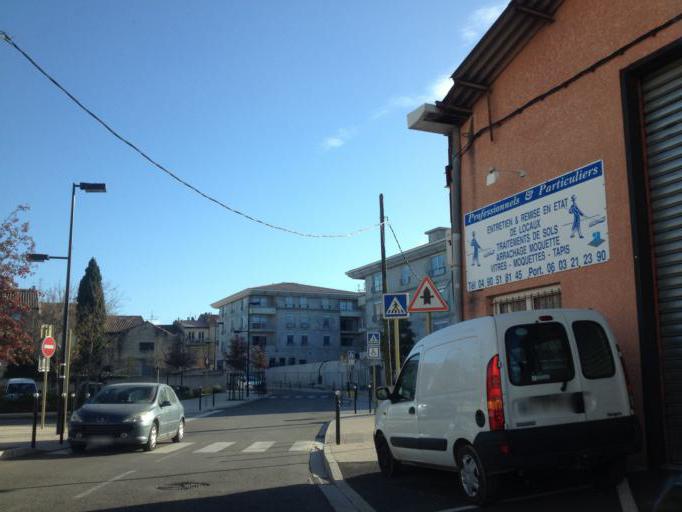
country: FR
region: Provence-Alpes-Cote d'Azur
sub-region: Departement du Vaucluse
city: Orange
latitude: 44.1406
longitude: 4.8040
